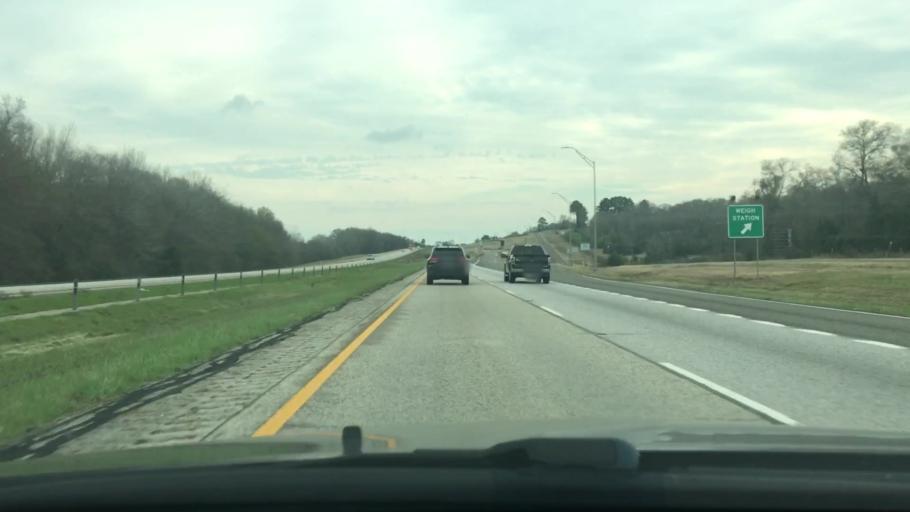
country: US
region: Texas
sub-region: Leon County
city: Centerville
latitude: 31.2832
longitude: -95.9925
